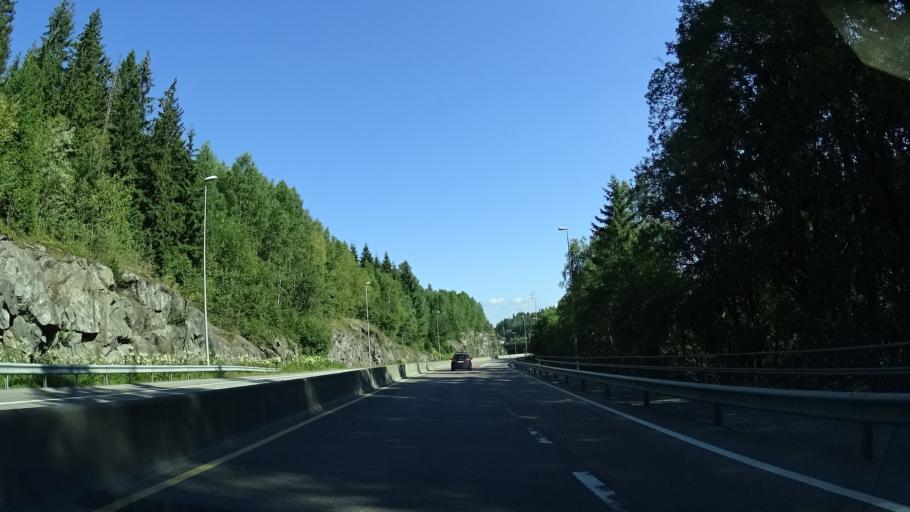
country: NO
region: Akershus
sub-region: Ski
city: Ski
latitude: 59.7374
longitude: 10.7823
